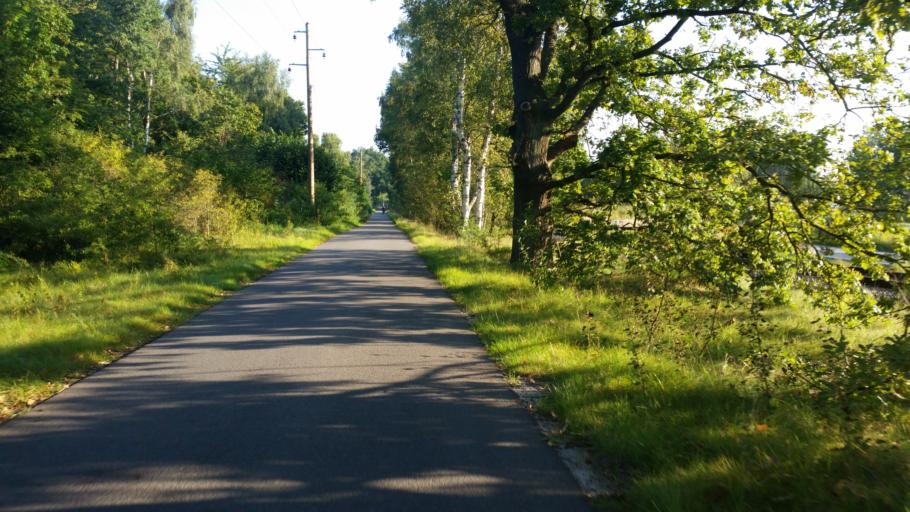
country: DE
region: Lower Saxony
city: Tappenbeck
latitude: 52.4323
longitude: 10.7418
